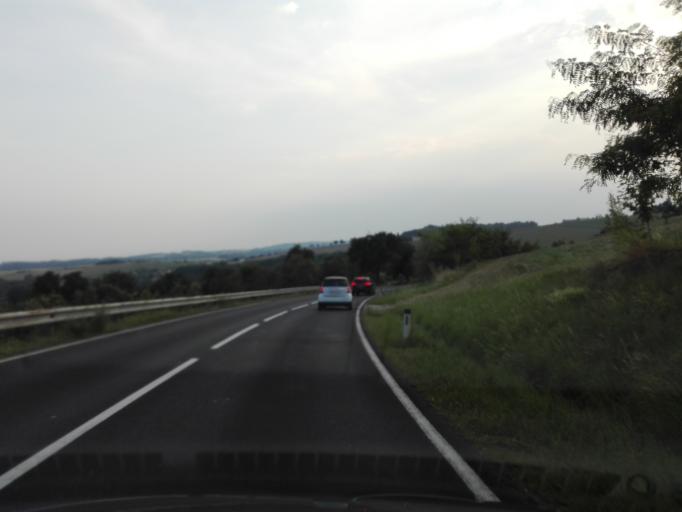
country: AT
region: Upper Austria
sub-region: Politischer Bezirk Grieskirchen
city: Grieskirchen
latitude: 48.2586
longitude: 13.8140
